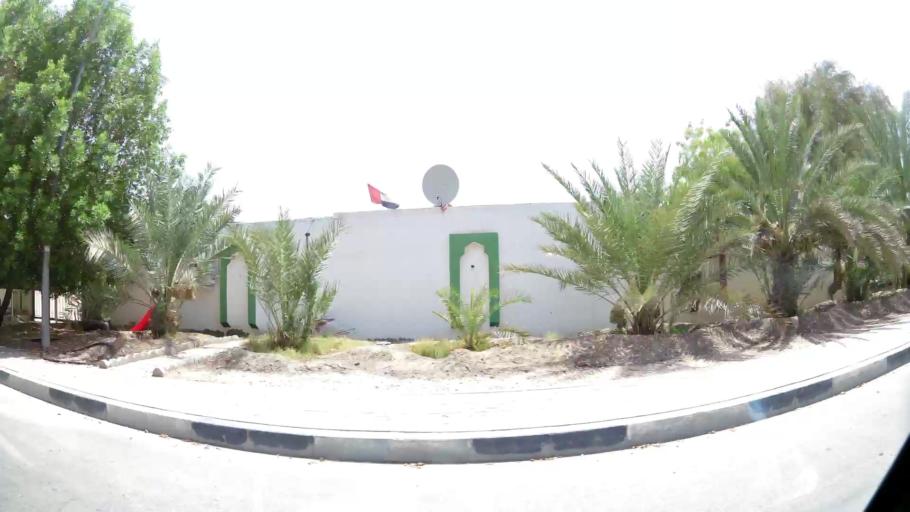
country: AE
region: Abu Dhabi
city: Al Ain
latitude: 24.1798
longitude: 55.7237
